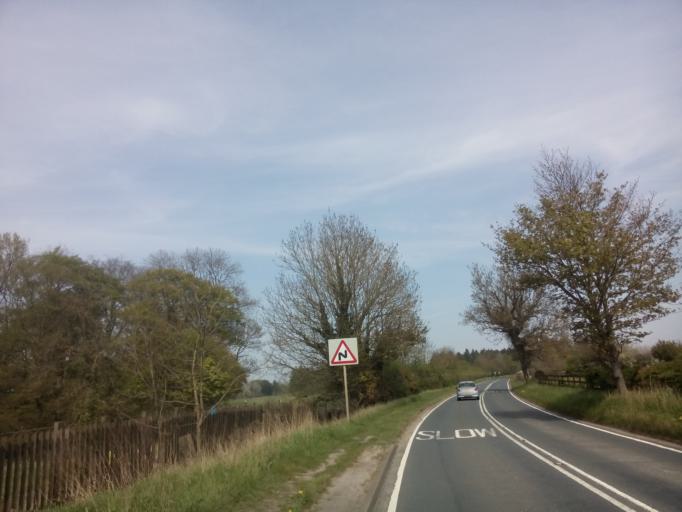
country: GB
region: England
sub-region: County Durham
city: West Rainton
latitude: 54.7928
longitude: -1.5131
